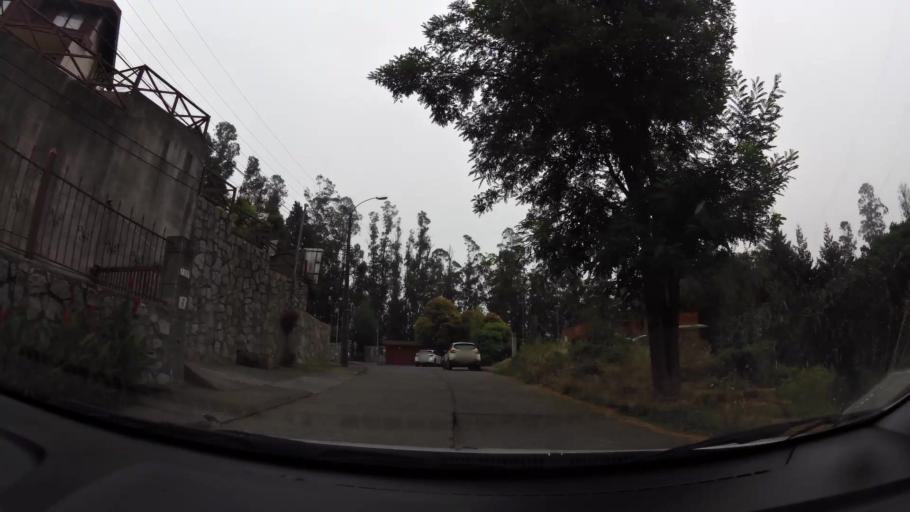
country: CL
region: Biobio
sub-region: Provincia de Concepcion
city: Concepcion
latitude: -36.8237
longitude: -73.0324
